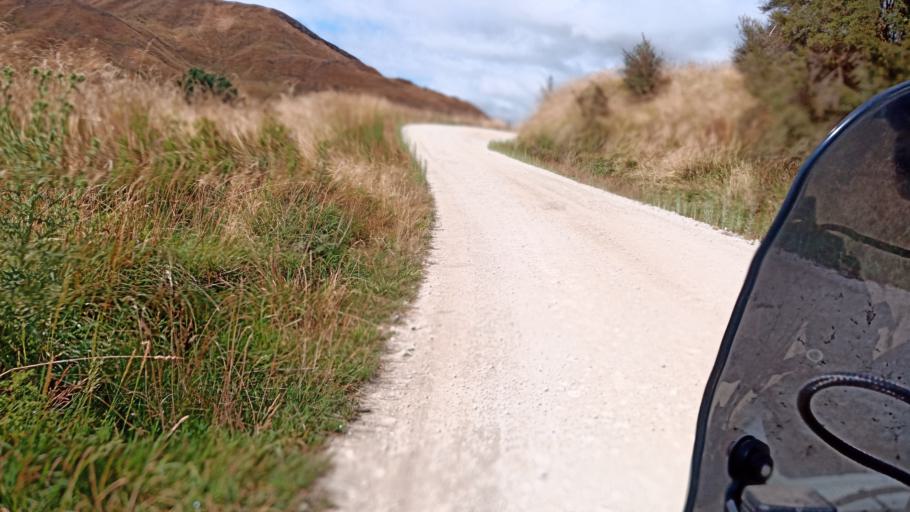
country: NZ
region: Hawke's Bay
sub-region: Wairoa District
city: Wairoa
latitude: -38.6096
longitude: 177.4394
